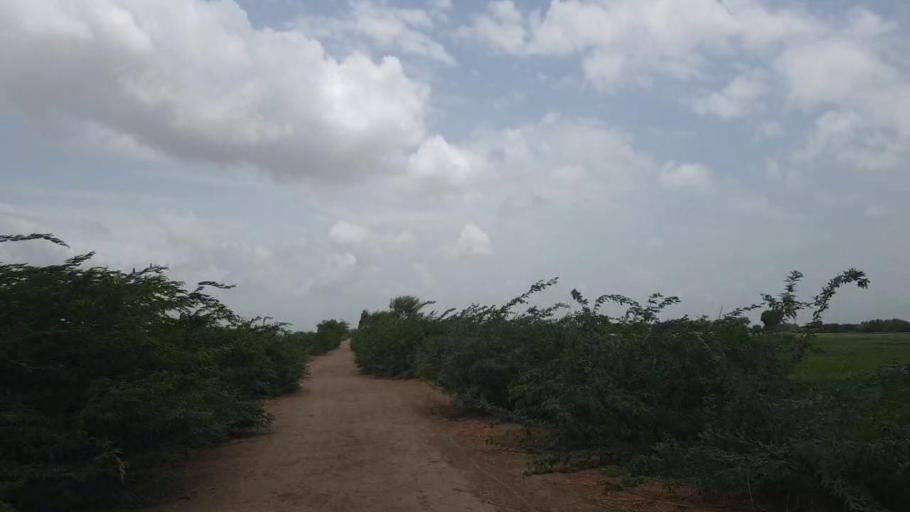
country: PK
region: Sindh
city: Badin
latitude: 24.6638
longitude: 68.8927
